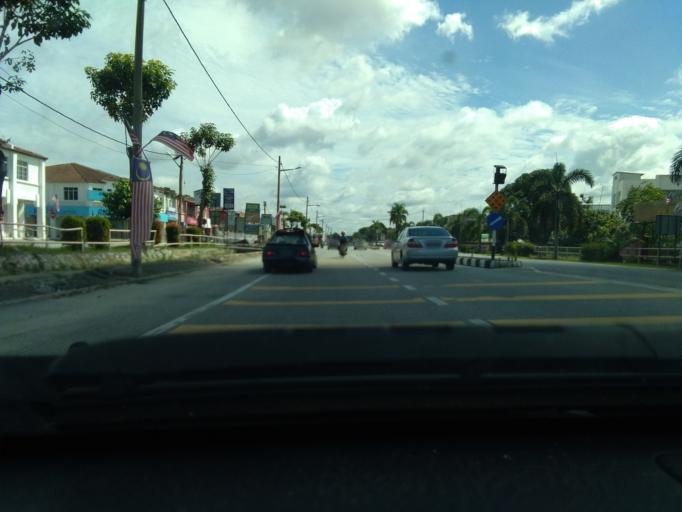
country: MY
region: Perak
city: Parit Buntar
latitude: 5.1128
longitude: 100.4829
